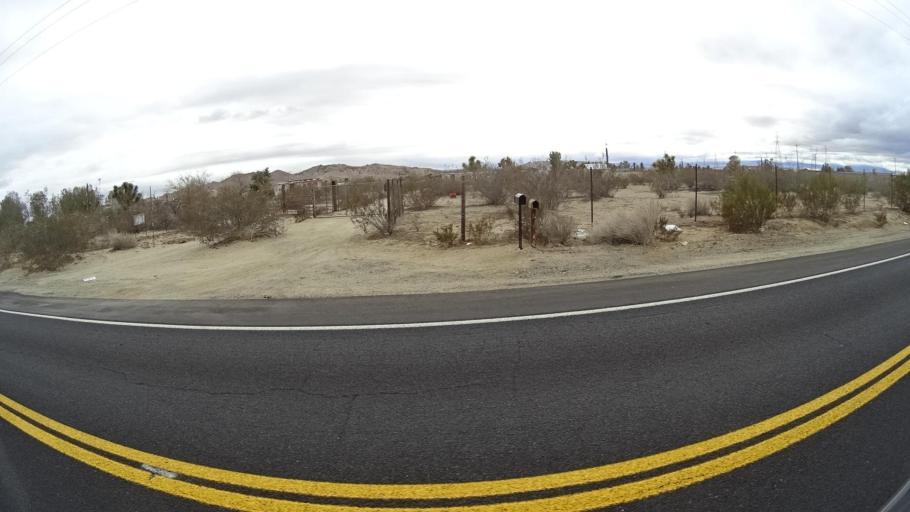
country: US
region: California
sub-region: Kern County
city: Rosamond
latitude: 34.9510
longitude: -118.2552
